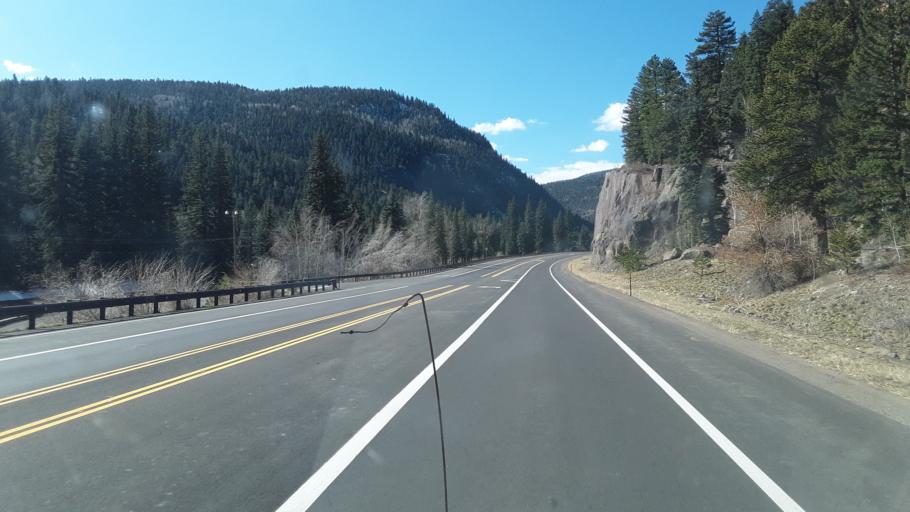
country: US
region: Colorado
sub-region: Mineral County
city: Creede
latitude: 37.6123
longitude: -106.7022
